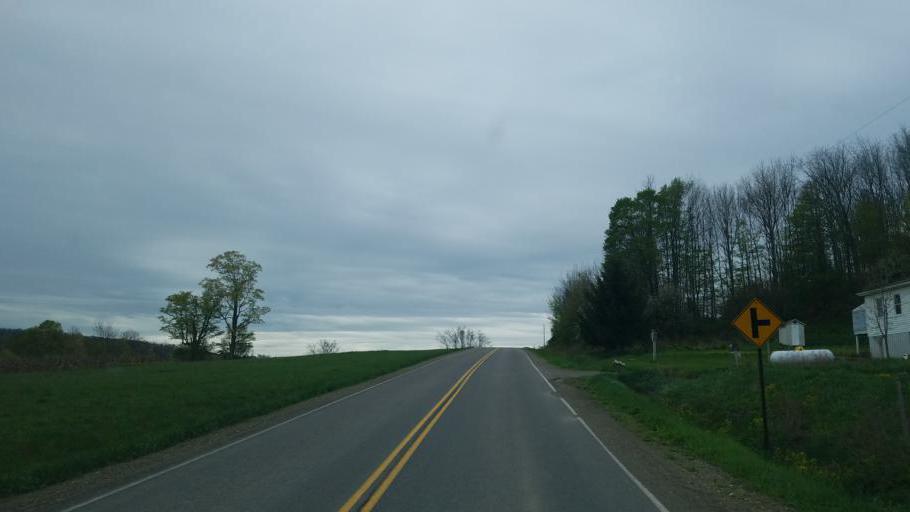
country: US
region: Pennsylvania
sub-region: Tioga County
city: Westfield
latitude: 42.0381
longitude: -77.4663
